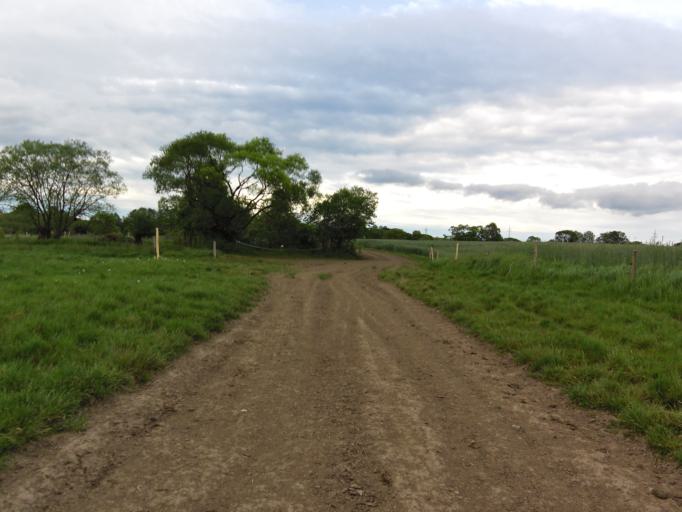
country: DE
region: Thuringia
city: Frauensee
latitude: 50.9203
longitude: 10.1021
